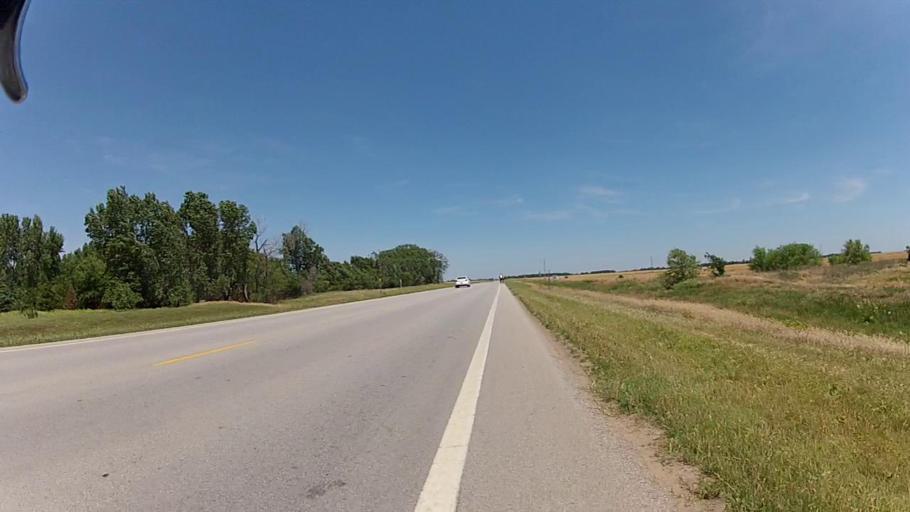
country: US
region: Kansas
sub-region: Harper County
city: Harper
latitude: 37.2388
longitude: -98.1501
